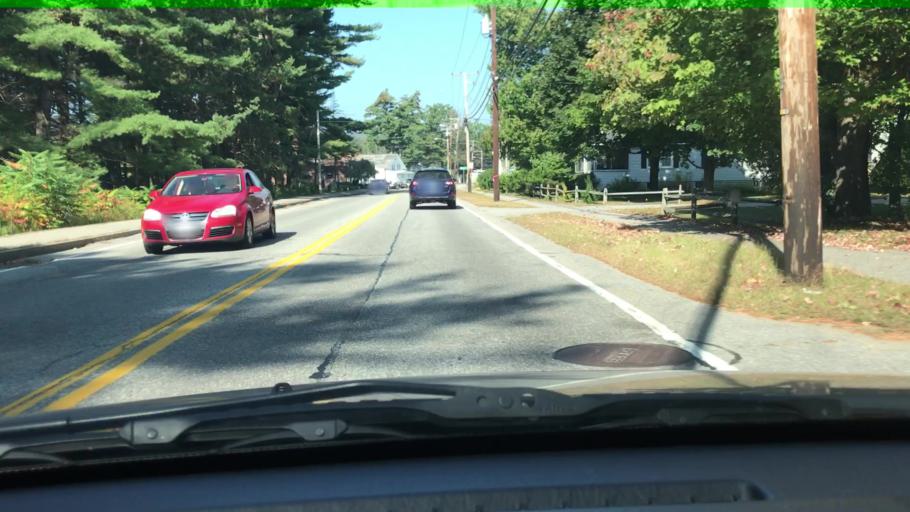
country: US
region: New Hampshire
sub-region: Cheshire County
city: Keene
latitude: 42.9416
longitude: -72.3096
